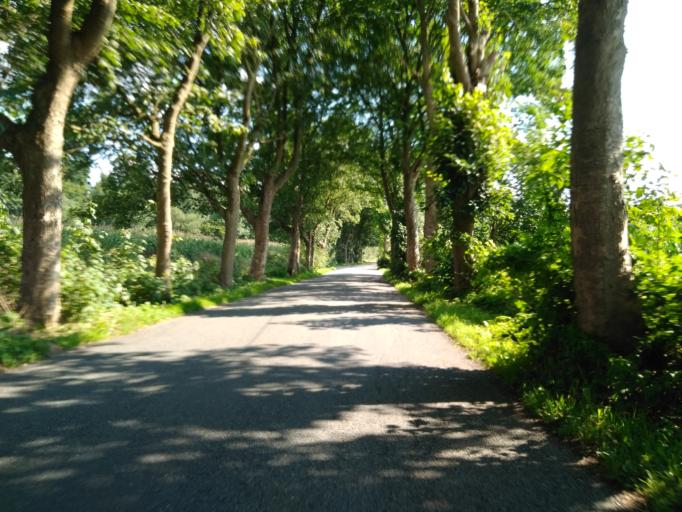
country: DE
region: North Rhine-Westphalia
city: Dorsten
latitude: 51.7364
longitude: 6.9726
